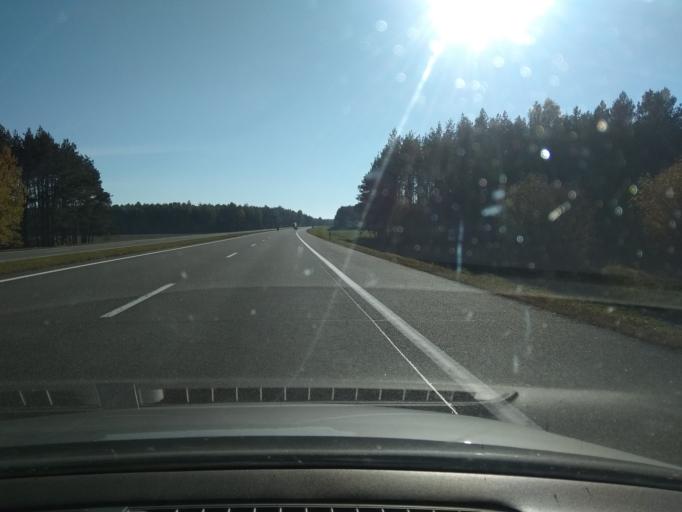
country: BY
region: Brest
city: Baranovichi
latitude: 53.0800
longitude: 25.8857
